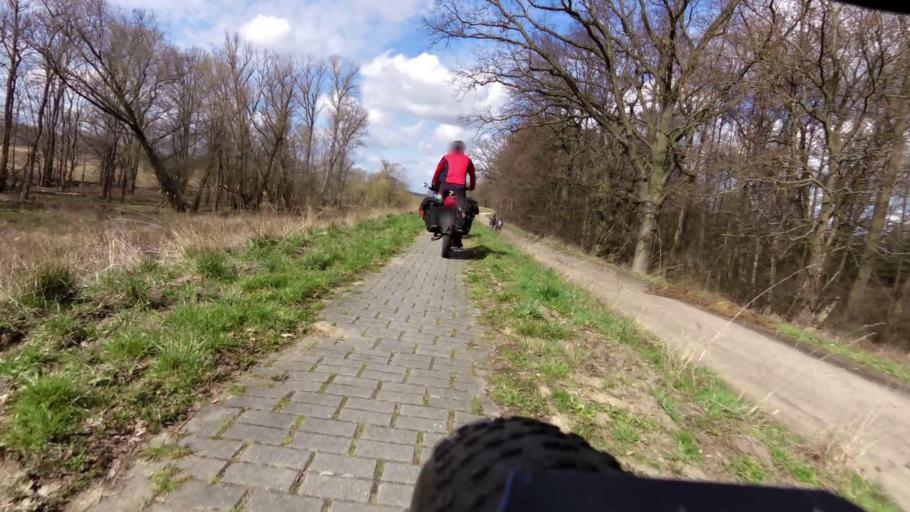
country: PL
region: Lubusz
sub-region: Powiat slubicki
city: Slubice
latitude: 52.3751
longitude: 14.5580
